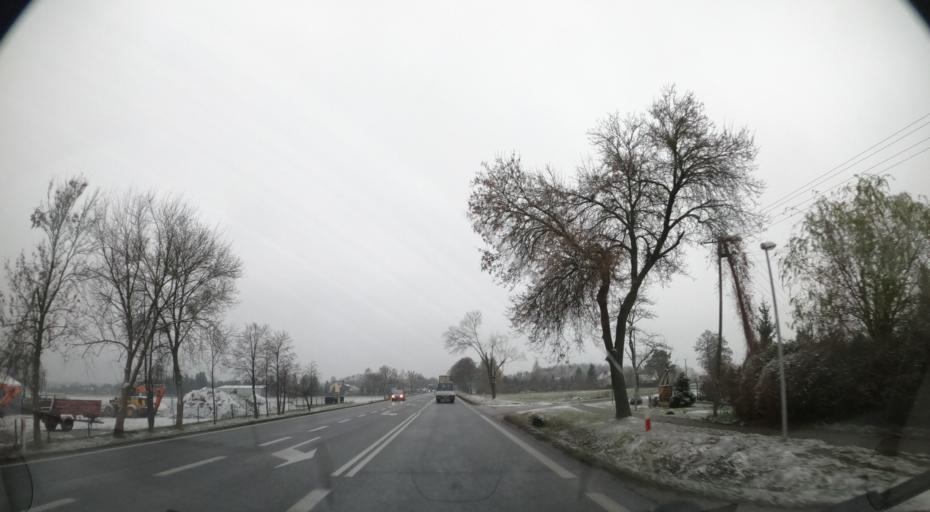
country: PL
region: Masovian Voivodeship
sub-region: Powiat sochaczewski
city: Teresin
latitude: 52.2148
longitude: 20.3987
